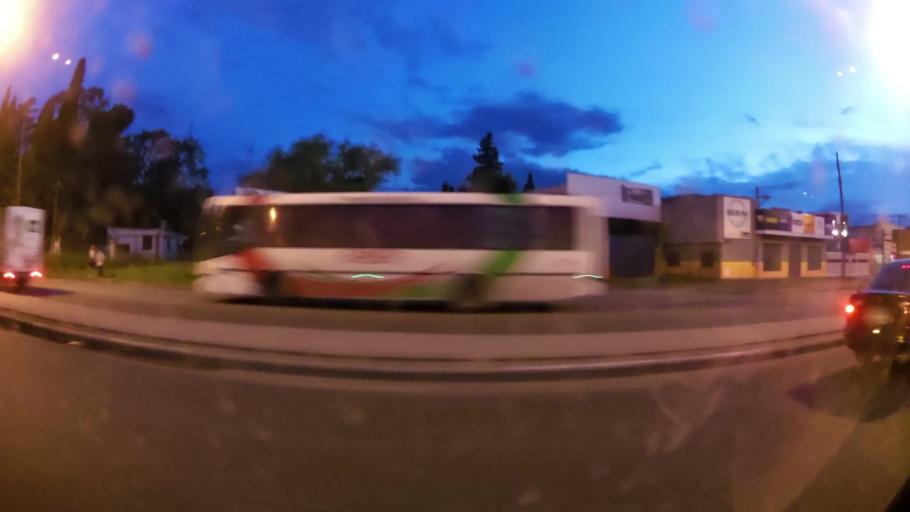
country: AR
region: Buenos Aires
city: San Nicolas de los Arroyos
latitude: -33.3521
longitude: -60.2400
